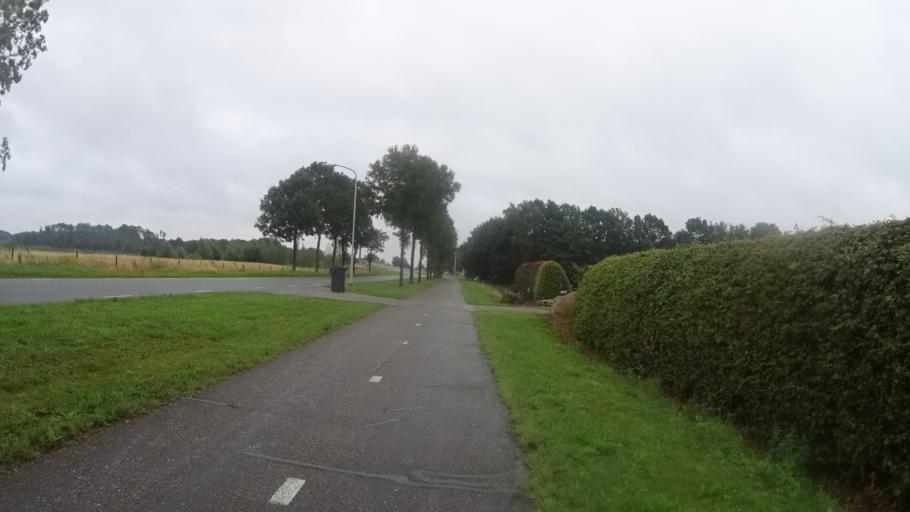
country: NL
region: Groningen
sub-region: Gemeente  Oldambt
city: Winschoten
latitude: 53.1547
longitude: 7.0629
